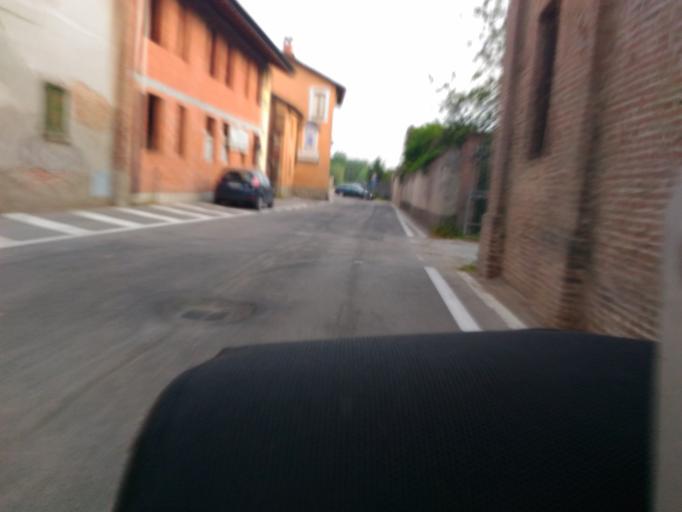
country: IT
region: Lombardy
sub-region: Provincia di Lodi
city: Tavazzano
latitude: 45.3368
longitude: 9.4043
